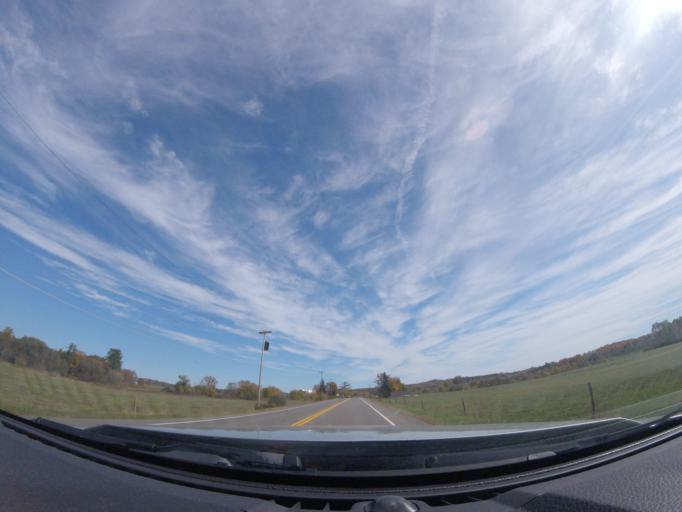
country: US
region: New York
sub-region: Tompkins County
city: Dryden
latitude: 42.5168
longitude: -76.3425
